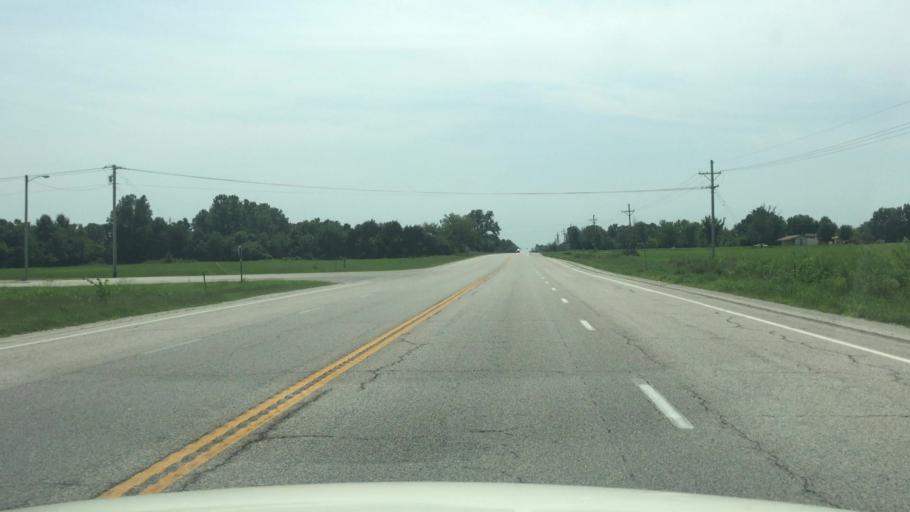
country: US
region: Kansas
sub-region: Cherokee County
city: Galena
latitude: 37.1218
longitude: -94.7044
